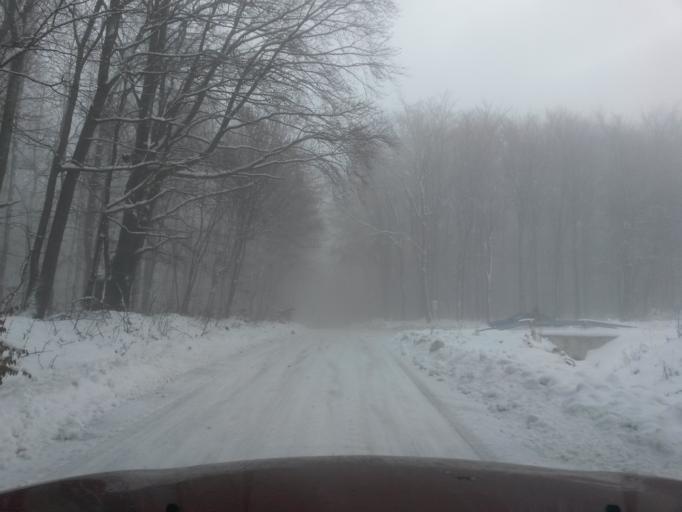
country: SK
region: Kosicky
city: Secovce
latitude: 48.8124
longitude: 21.5279
